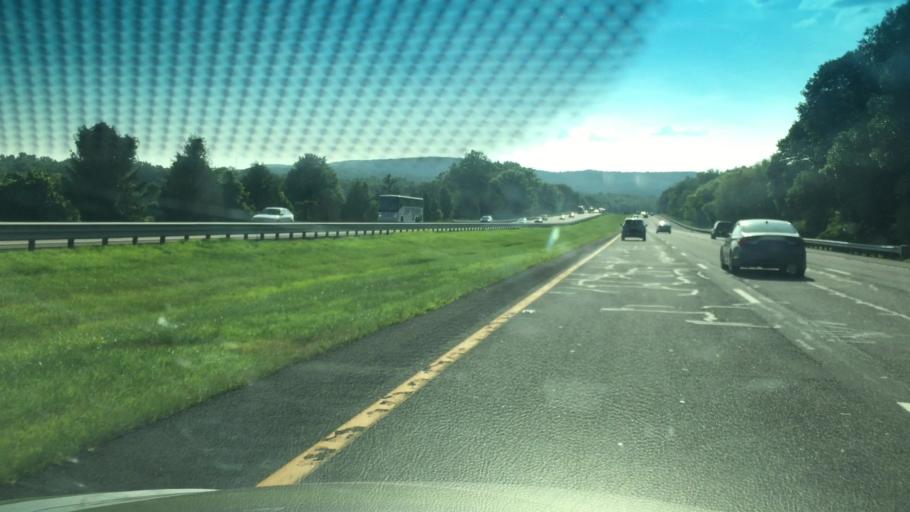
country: US
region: New Jersey
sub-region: Warren County
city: Hackettstown
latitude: 40.9222
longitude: -74.8608
